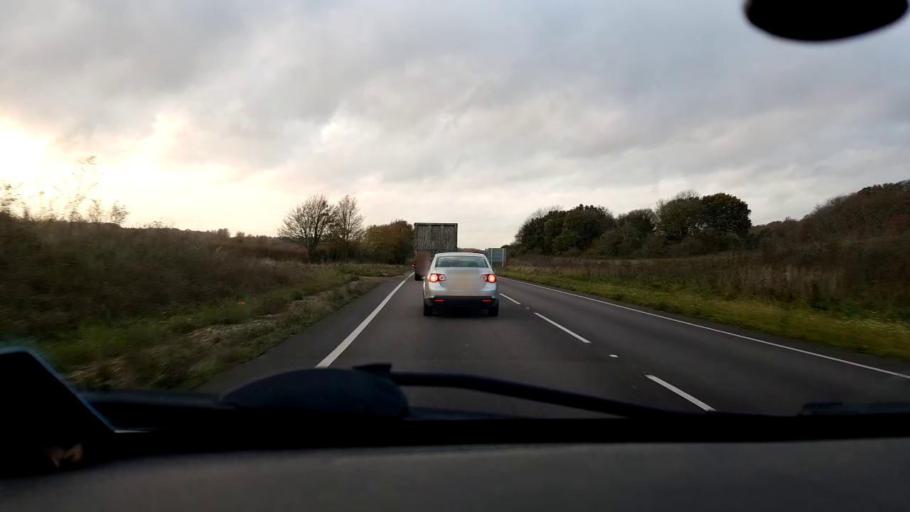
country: GB
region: England
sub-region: Norfolk
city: Costessey
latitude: 52.6952
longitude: 1.1707
